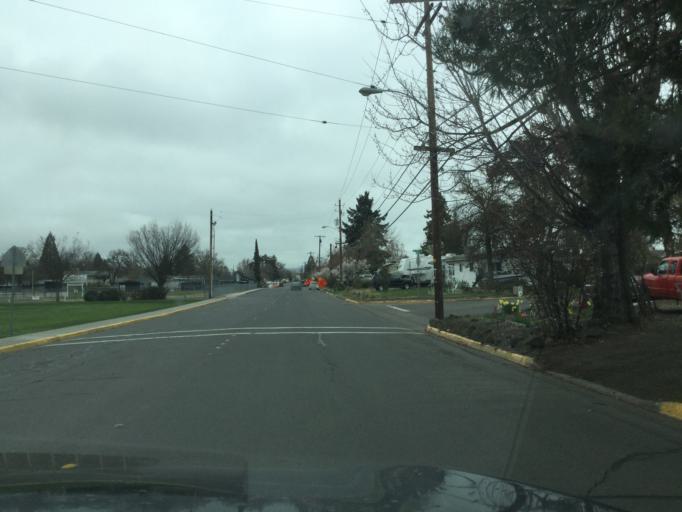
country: US
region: Oregon
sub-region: Jackson County
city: Central Point
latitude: 42.3800
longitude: -122.9196
